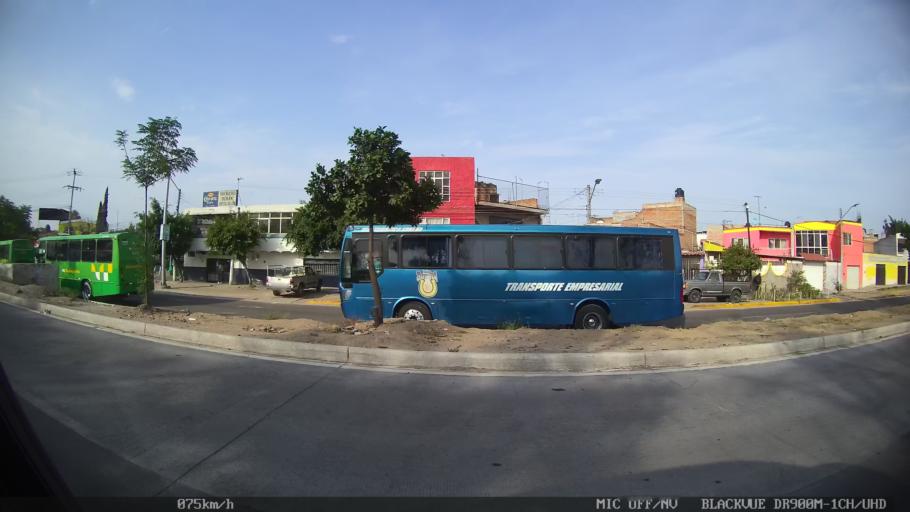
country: MX
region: Jalisco
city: Tlaquepaque
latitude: 20.6982
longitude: -103.2762
